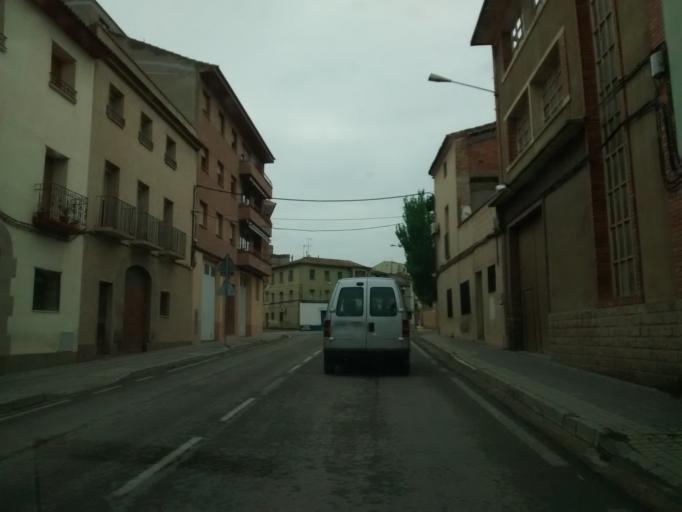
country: ES
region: Aragon
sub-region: Provincia de Zaragoza
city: Caspe
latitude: 41.2324
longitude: -0.0398
